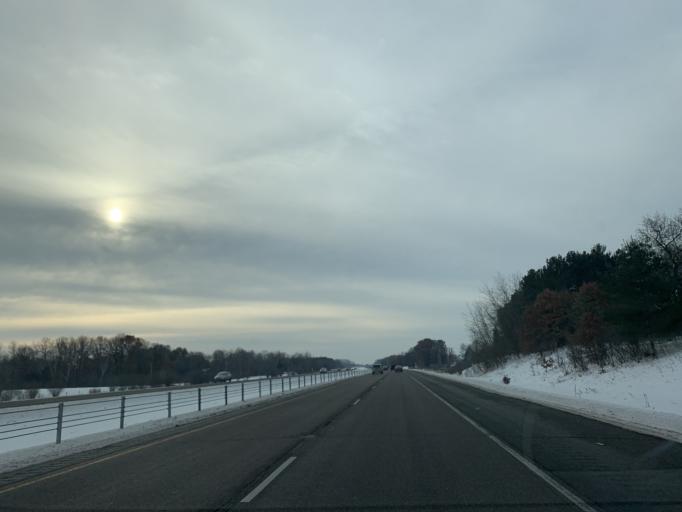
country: US
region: Minnesota
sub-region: Chisago County
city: Wyoming
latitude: 45.3144
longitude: -93.0037
